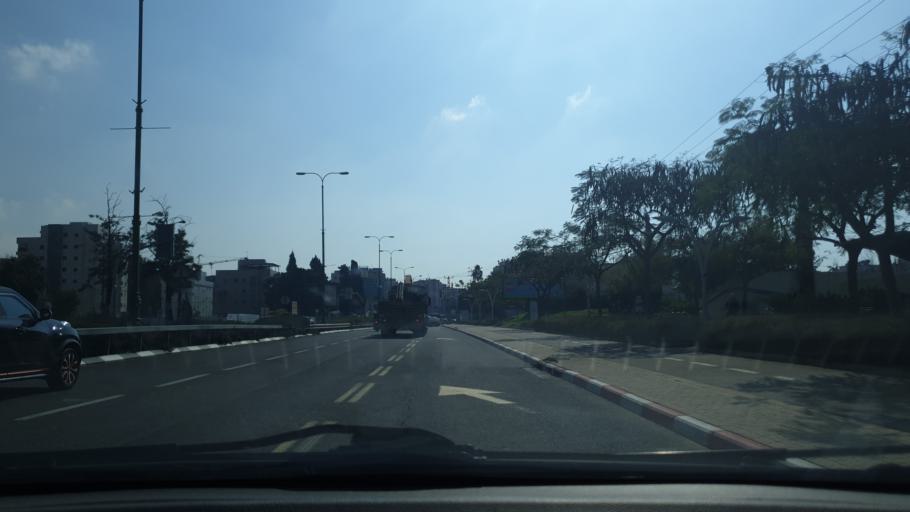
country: IL
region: Central District
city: Rishon LeZiyyon
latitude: 31.9749
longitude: 34.8069
